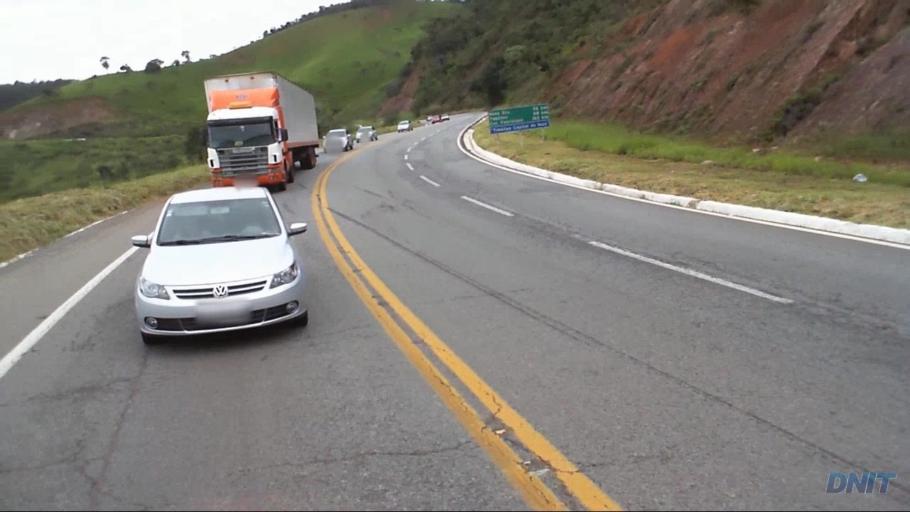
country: BR
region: Minas Gerais
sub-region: Joao Monlevade
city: Joao Monlevade
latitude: -19.8490
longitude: -43.2482
